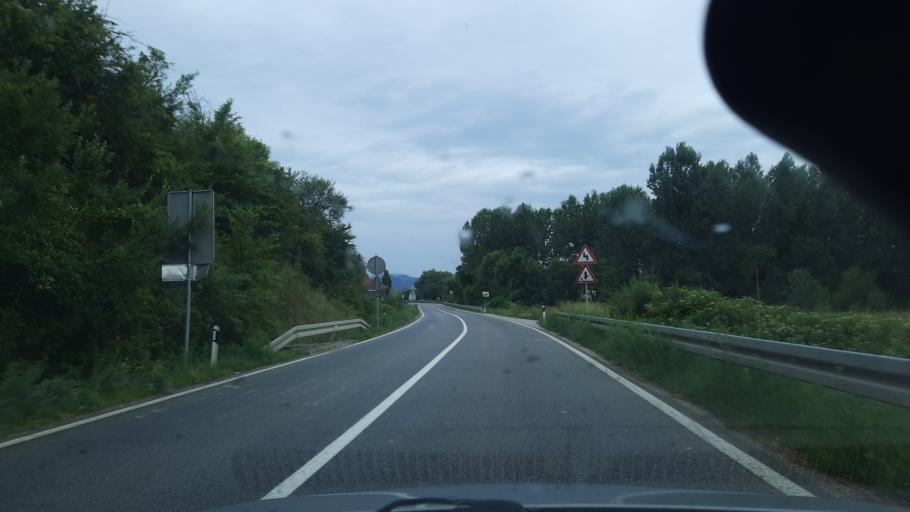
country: RS
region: Central Serbia
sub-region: Sumadijski Okrug
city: Knic
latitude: 43.8941
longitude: 20.7701
